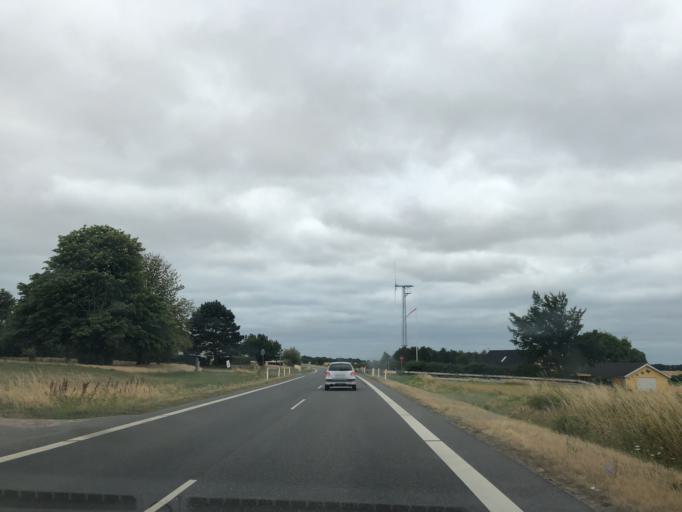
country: DK
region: Zealand
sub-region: Slagelse Kommune
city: Skaelskor
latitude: 55.2394
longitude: 11.3161
